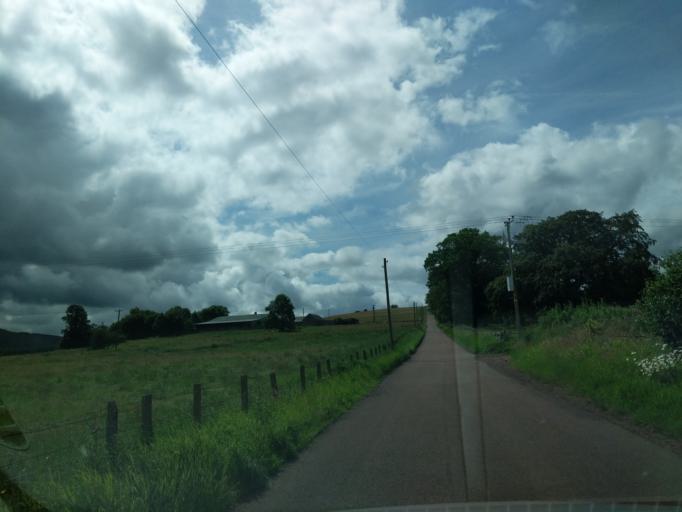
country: GB
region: Scotland
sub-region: South Lanarkshire
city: Carnwath
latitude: 55.6290
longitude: -3.6734
